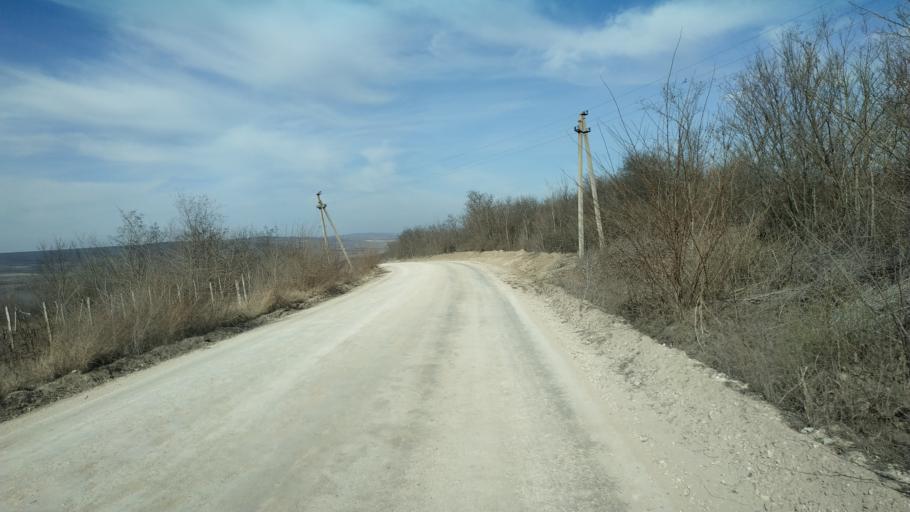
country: MD
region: Nisporeni
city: Nisporeni
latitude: 46.9686
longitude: 28.1996
